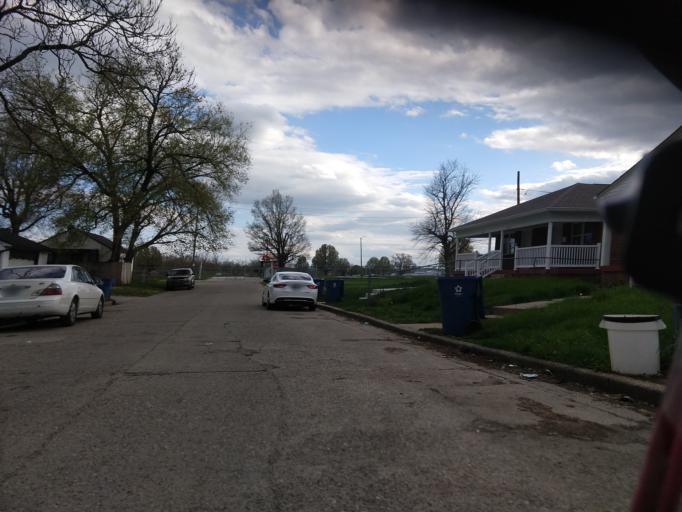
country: US
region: Indiana
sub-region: Marion County
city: Broad Ripple
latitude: 39.8336
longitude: -86.1276
